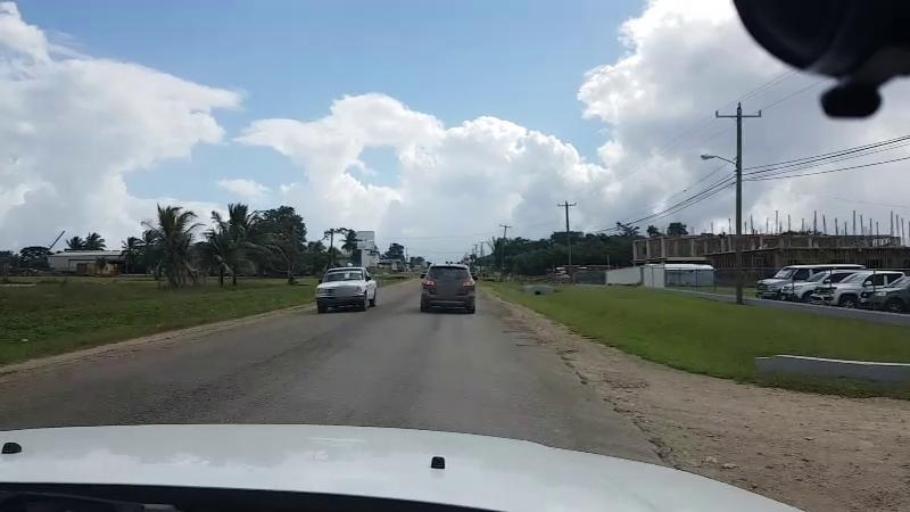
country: BZ
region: Cayo
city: Belmopan
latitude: 17.2492
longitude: -88.7845
